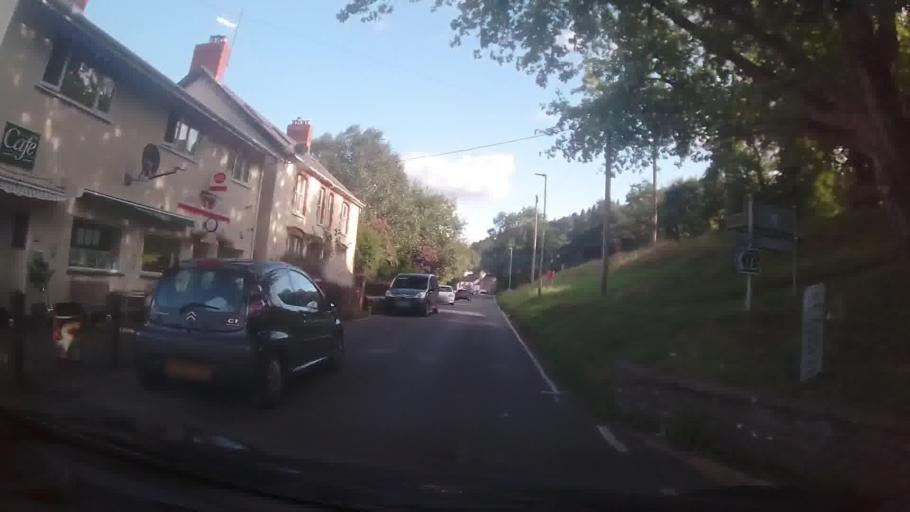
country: GB
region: Wales
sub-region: Sir Powys
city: Brecon
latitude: 51.8962
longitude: -3.2907
